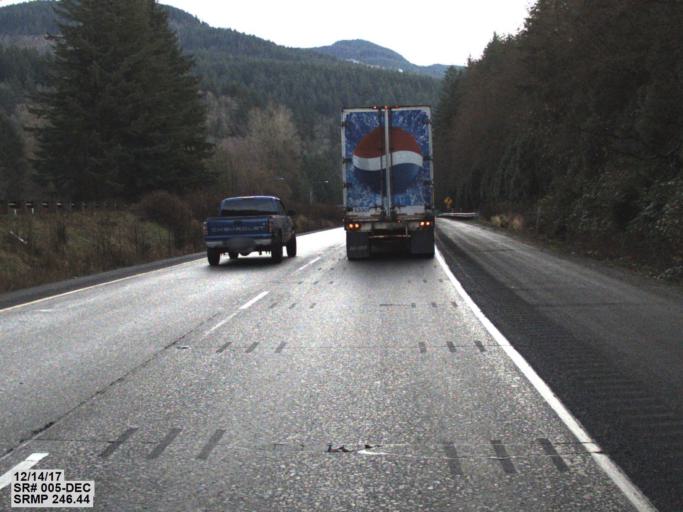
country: US
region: Washington
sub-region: Whatcom County
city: Geneva
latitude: 48.6890
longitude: -122.4032
